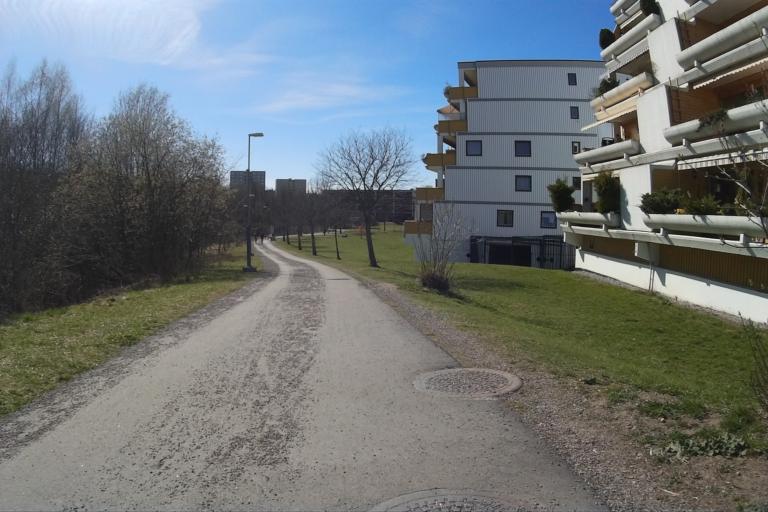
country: NO
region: Oslo
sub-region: Oslo
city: Oslo
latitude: 59.9074
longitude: 10.8059
